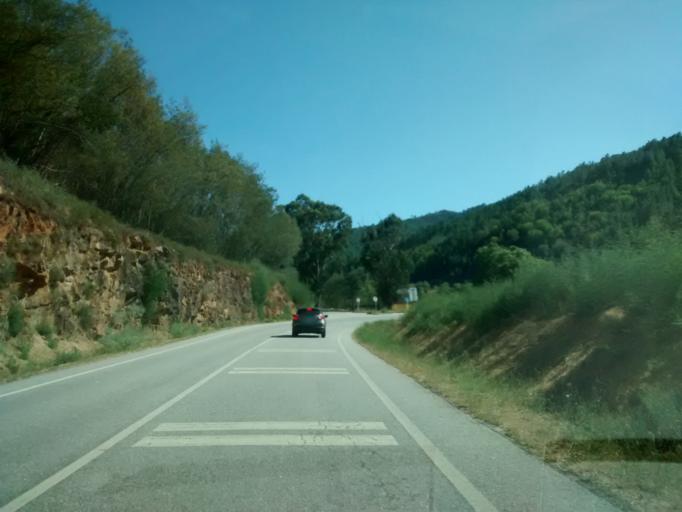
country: PT
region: Castelo Branco
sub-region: Belmonte
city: Belmonte
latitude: 40.4024
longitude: -7.3958
